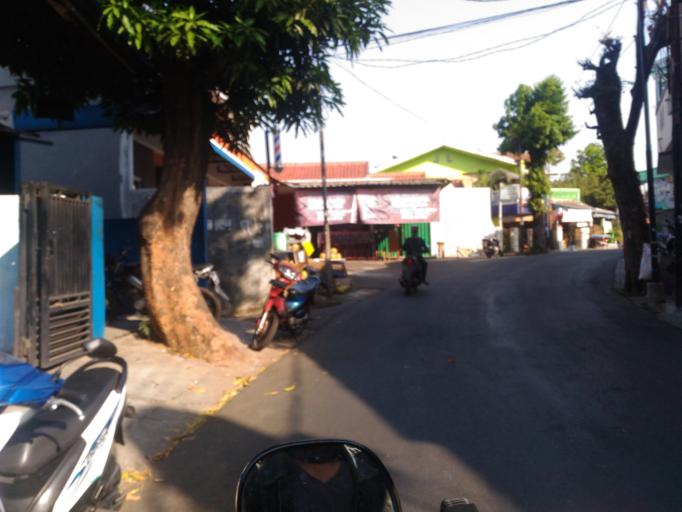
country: ID
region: West Java
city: Depok
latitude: -6.3260
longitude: 106.8520
